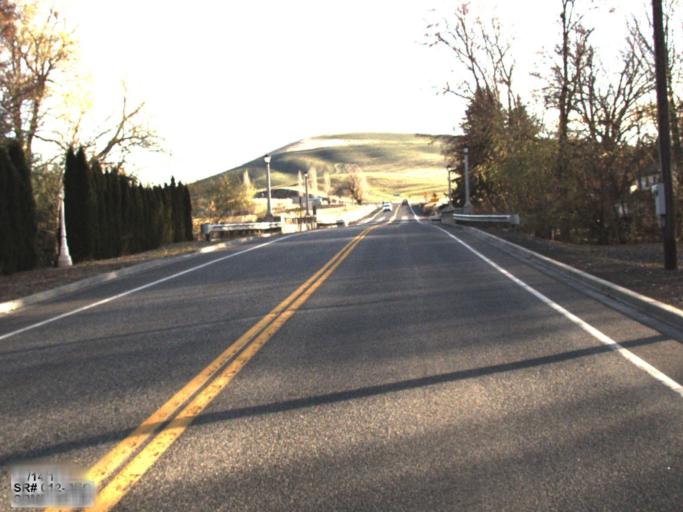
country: US
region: Washington
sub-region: Walla Walla County
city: Waitsburg
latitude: 46.2628
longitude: -118.1532
